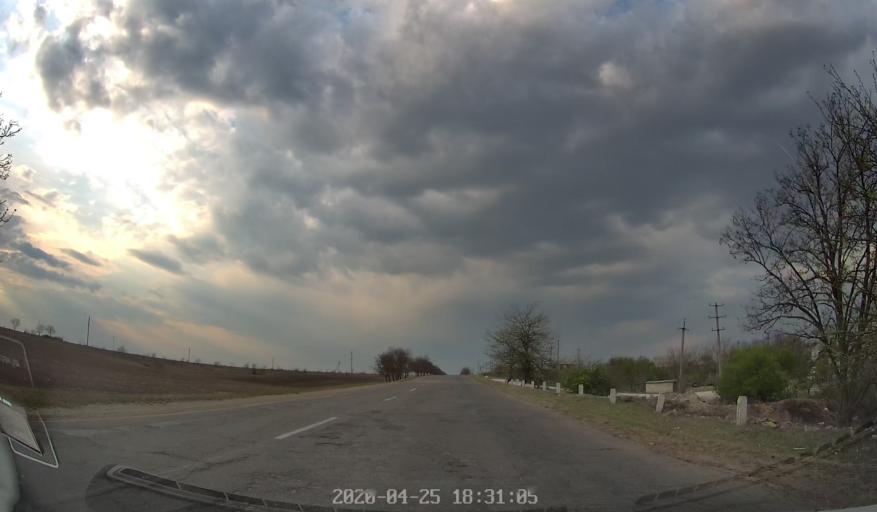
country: MD
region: Criuleni
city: Criuleni
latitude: 47.2133
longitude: 29.1485
